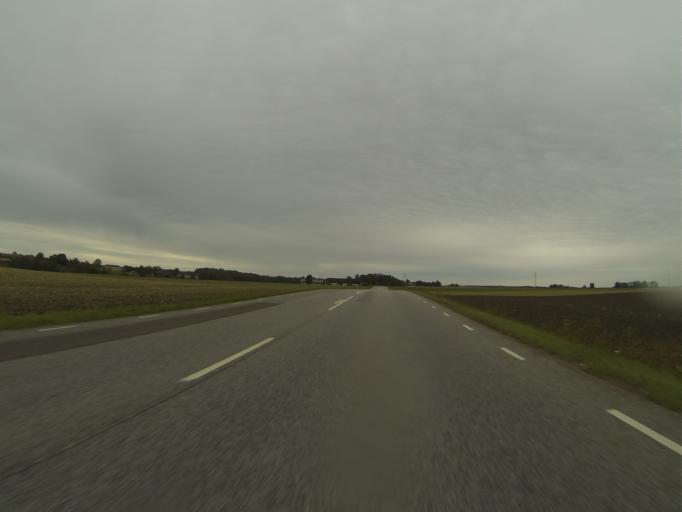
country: SE
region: Skane
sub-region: Svedala Kommun
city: Klagerup
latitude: 55.6287
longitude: 13.2969
